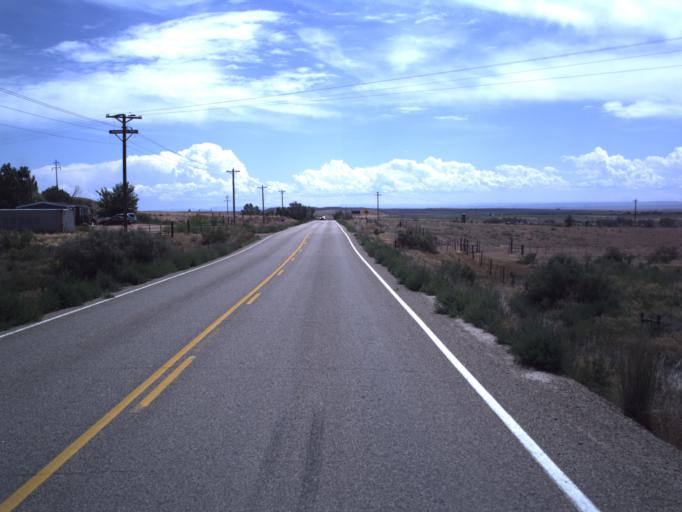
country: US
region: Utah
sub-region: Uintah County
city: Maeser
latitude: 40.2183
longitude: -109.6807
